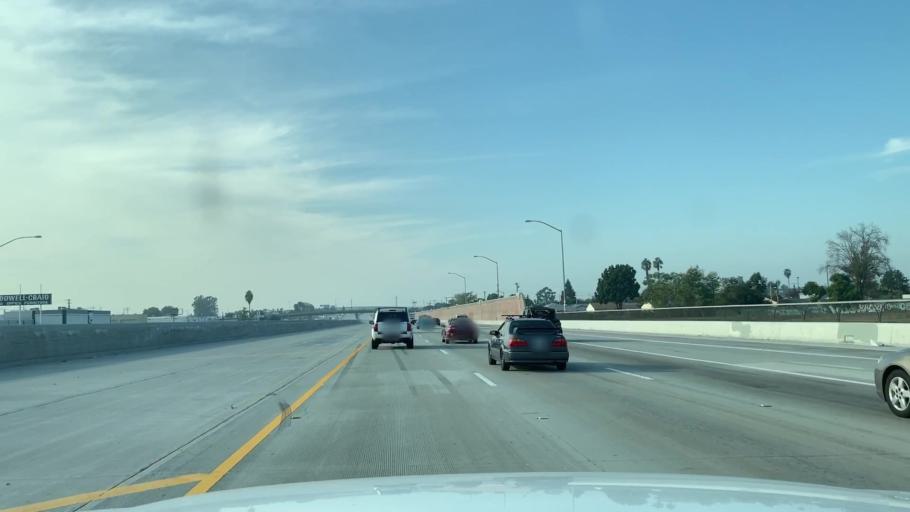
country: US
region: California
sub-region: Los Angeles County
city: Norwalk
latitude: 33.8958
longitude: -118.0501
